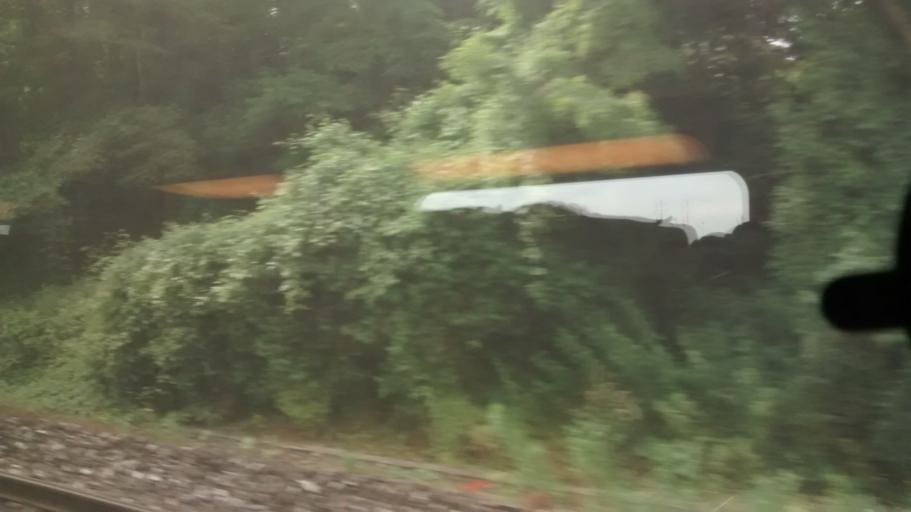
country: FR
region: Ile-de-France
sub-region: Departement du Val-de-Marne
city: Fresnes
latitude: 48.7453
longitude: 2.3204
